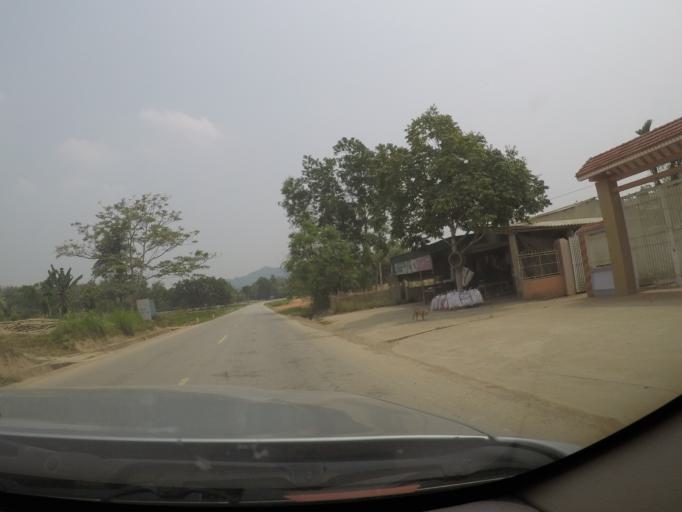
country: VN
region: Thanh Hoa
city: Thi Tran Yen Cat
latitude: 19.7051
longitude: 105.4471
